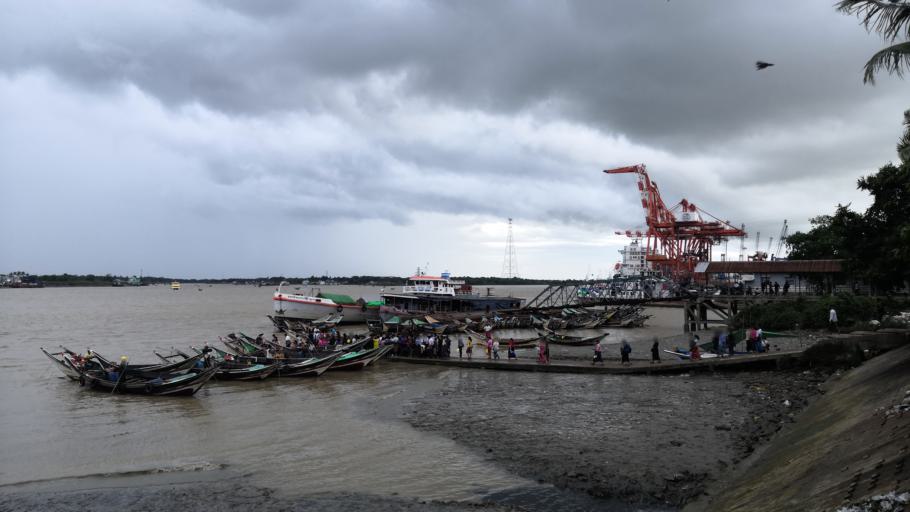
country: MM
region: Yangon
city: Yangon
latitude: 16.7735
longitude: 96.1398
